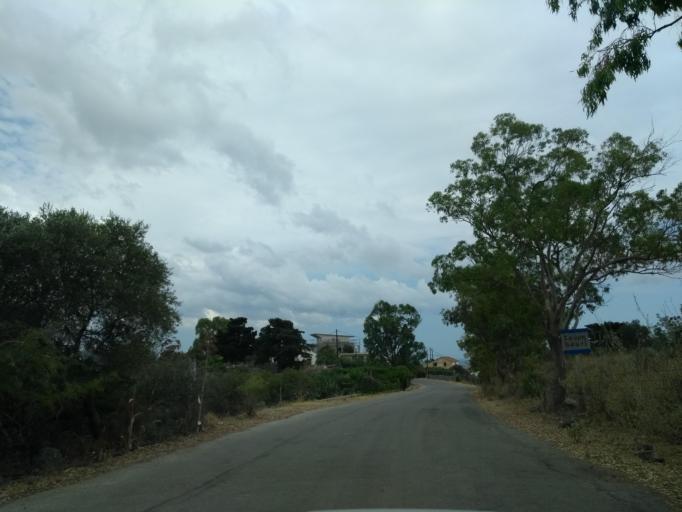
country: GR
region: Crete
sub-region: Nomos Chanias
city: Georgioupolis
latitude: 35.3945
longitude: 24.2358
